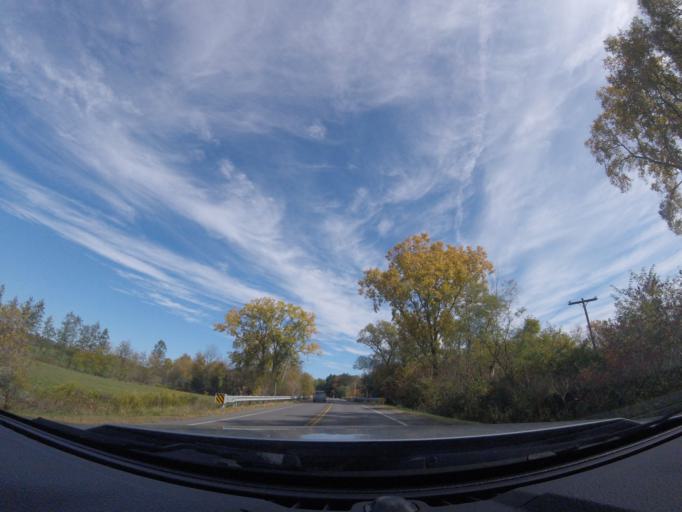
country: US
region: New York
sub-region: Tompkins County
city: Dryden
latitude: 42.5199
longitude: -76.3283
